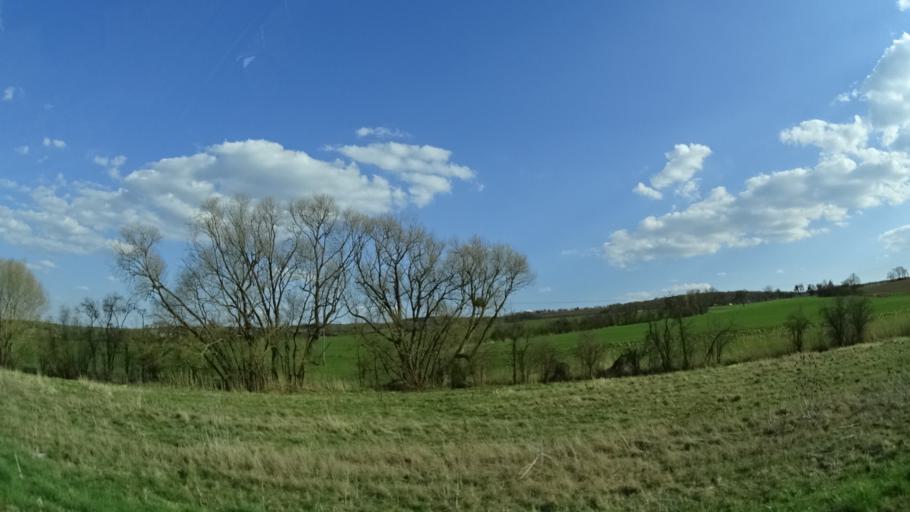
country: DE
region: Rheinland-Pfalz
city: Meddersheim
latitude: 49.7734
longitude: 7.6055
